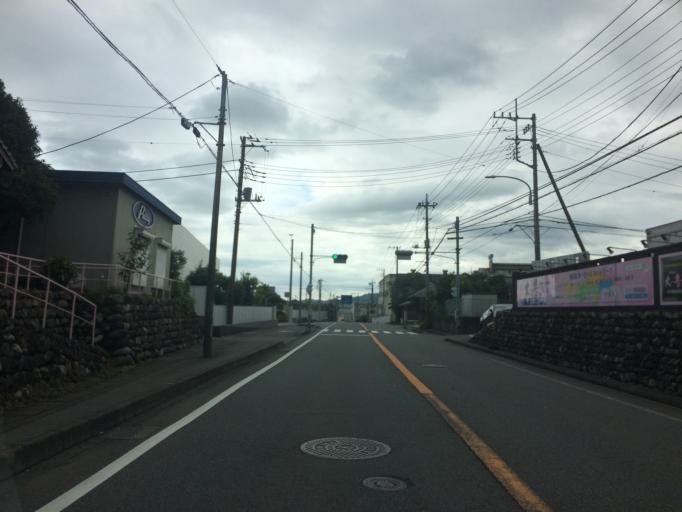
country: JP
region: Shizuoka
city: Fuji
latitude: 35.1855
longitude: 138.6504
